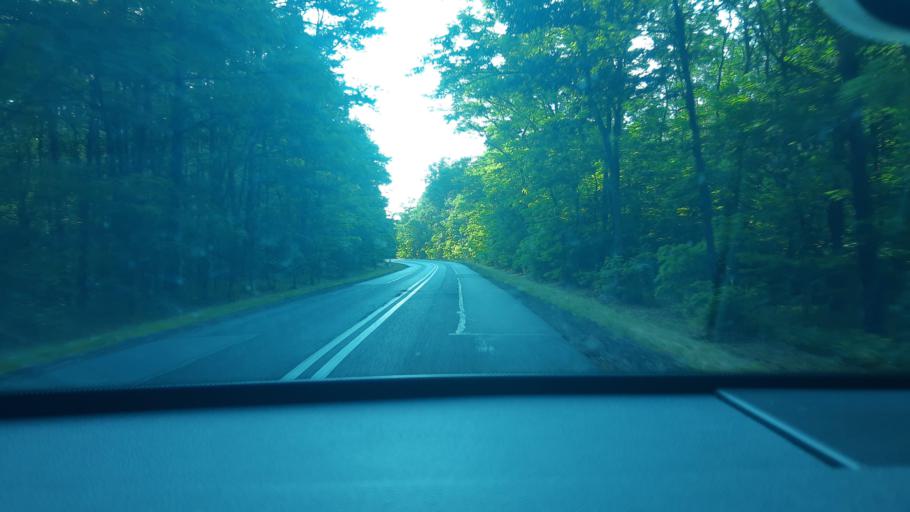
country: PL
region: Lodz Voivodeship
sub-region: Powiat sieradzki
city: Burzenin
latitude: 51.5151
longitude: 18.8010
